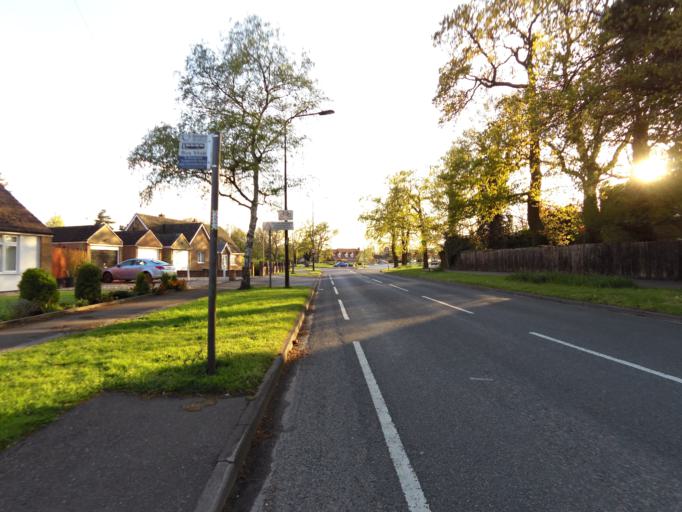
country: GB
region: England
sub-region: Suffolk
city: Ipswich
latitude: 52.0716
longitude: 1.1719
